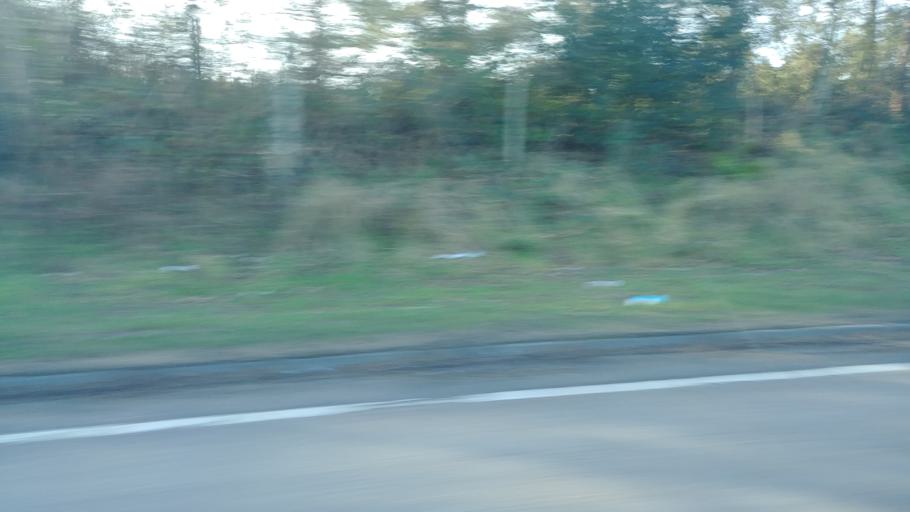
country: GB
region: Northern Ireland
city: Hillsborough
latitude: 54.4910
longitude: -6.0714
